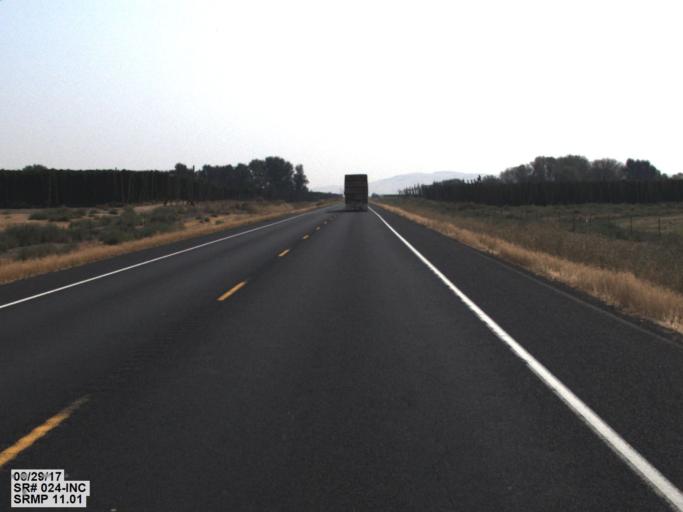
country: US
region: Washington
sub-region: Yakima County
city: Zillah
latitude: 46.5291
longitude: -120.2681
